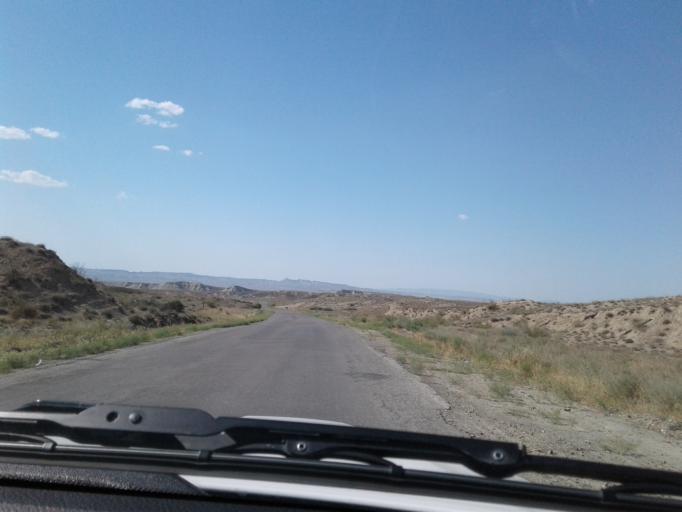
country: TM
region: Balkan
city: Magtymguly
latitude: 38.5049
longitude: 56.1926
